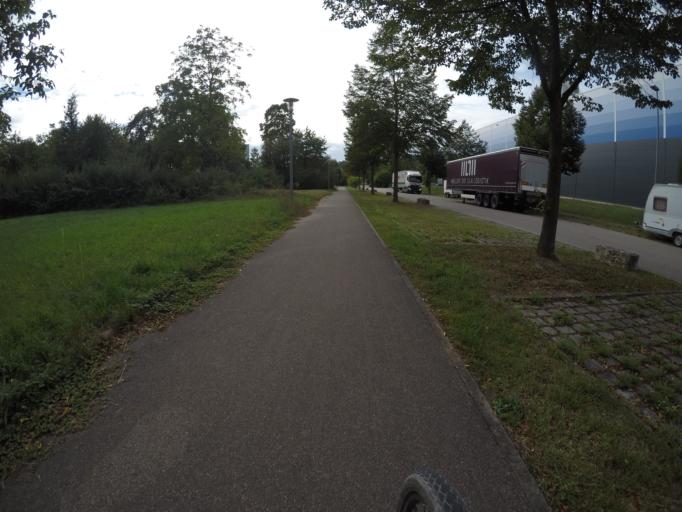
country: DE
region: Baden-Wuerttemberg
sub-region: Regierungsbezirk Stuttgart
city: Benningen am Neckar
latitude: 48.9261
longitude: 9.2325
